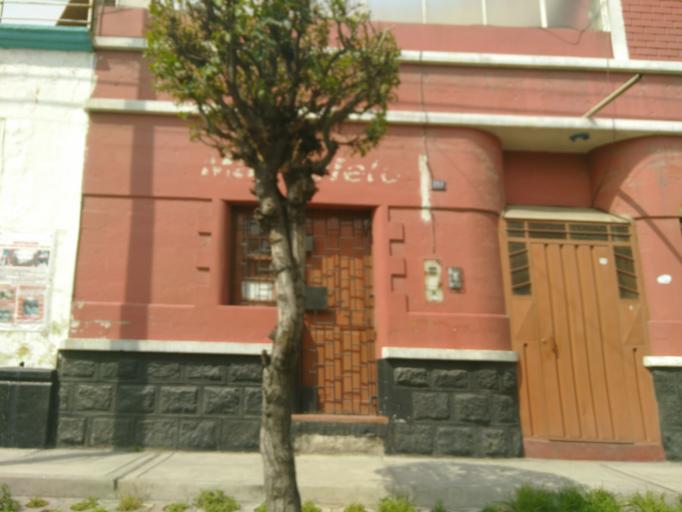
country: PE
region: Arequipa
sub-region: Provincia de Arequipa
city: Arequipa
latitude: -16.4094
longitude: -71.5385
